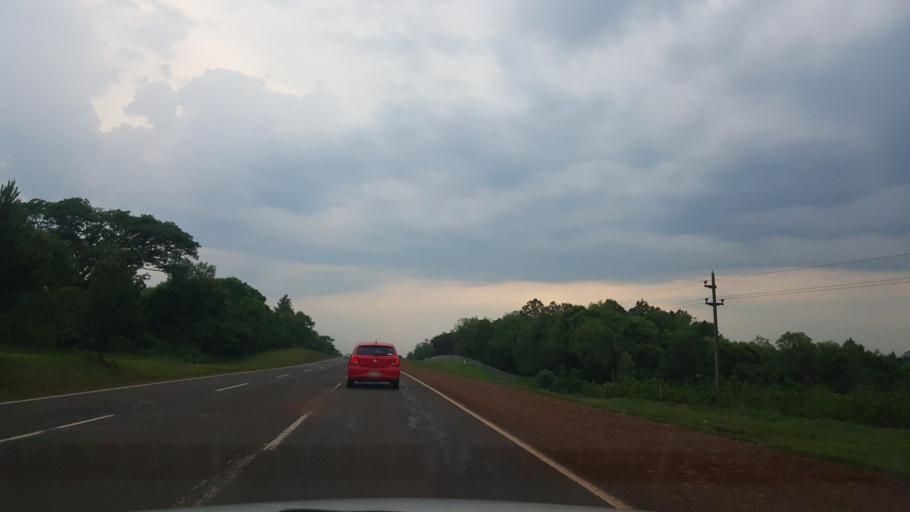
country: AR
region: Misiones
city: Santo Pipo
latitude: -27.1625
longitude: -55.4351
